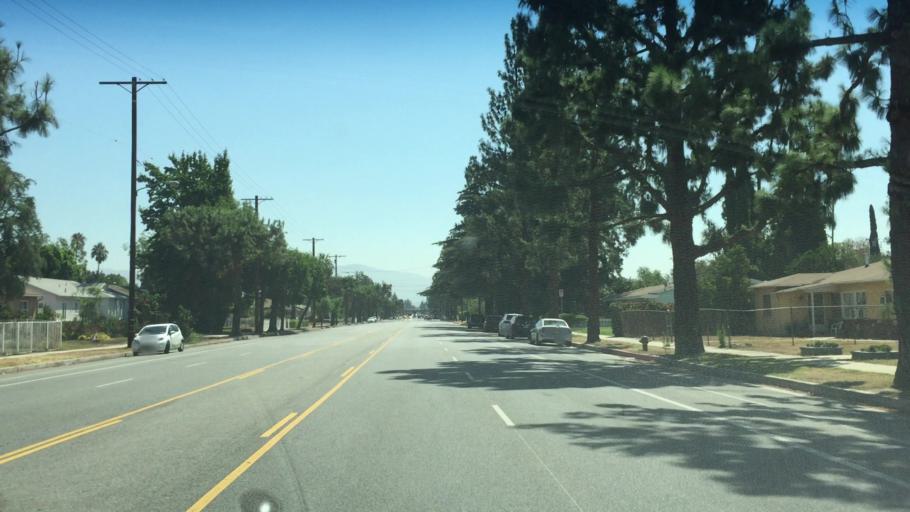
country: US
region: California
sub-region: Los Angeles County
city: San Fernando
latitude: 34.2573
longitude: -118.4804
